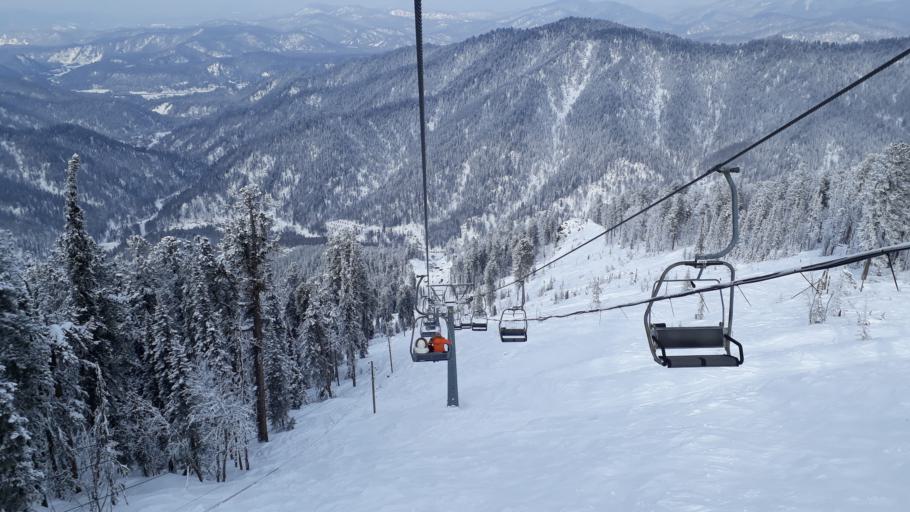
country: RU
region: Altay
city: Iogach
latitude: 51.7300
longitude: 87.3005
